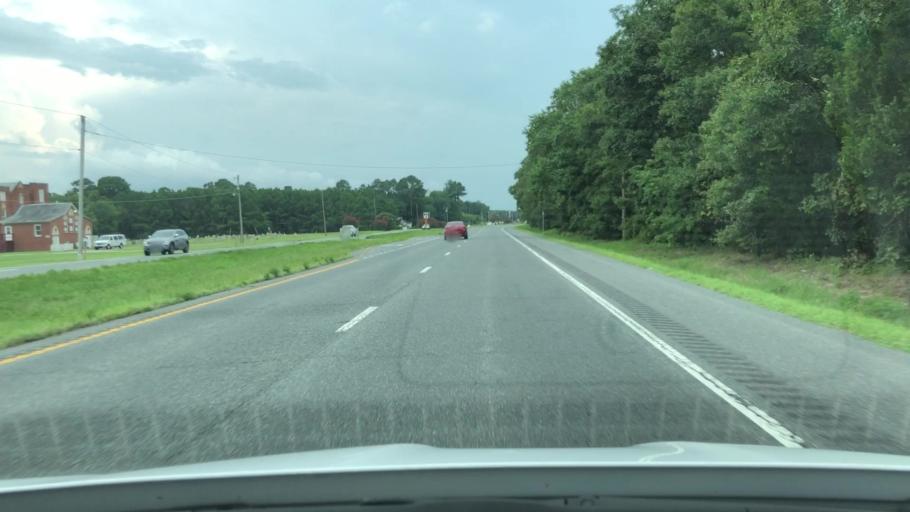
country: US
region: Virginia
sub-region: Northampton County
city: Eastville
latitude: 37.3733
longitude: -75.9249
